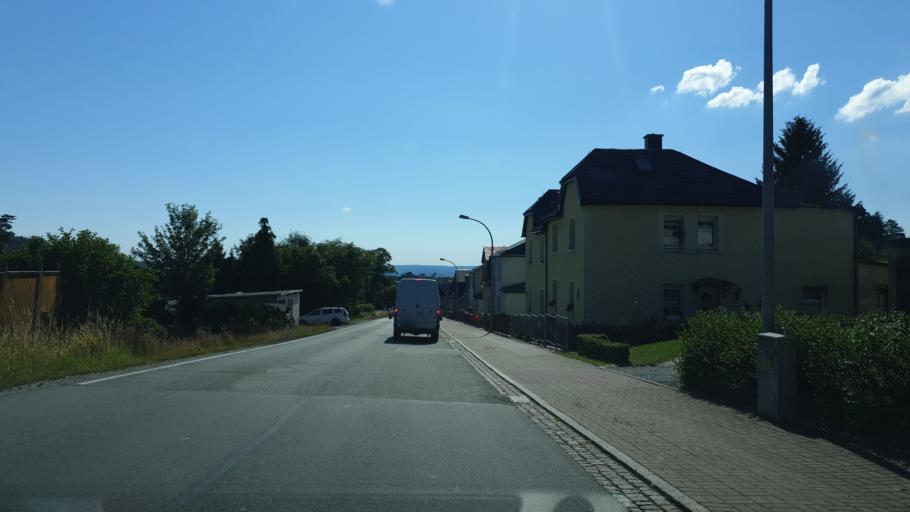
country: DE
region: Saxony
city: Geyer
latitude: 50.6252
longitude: 12.9109
